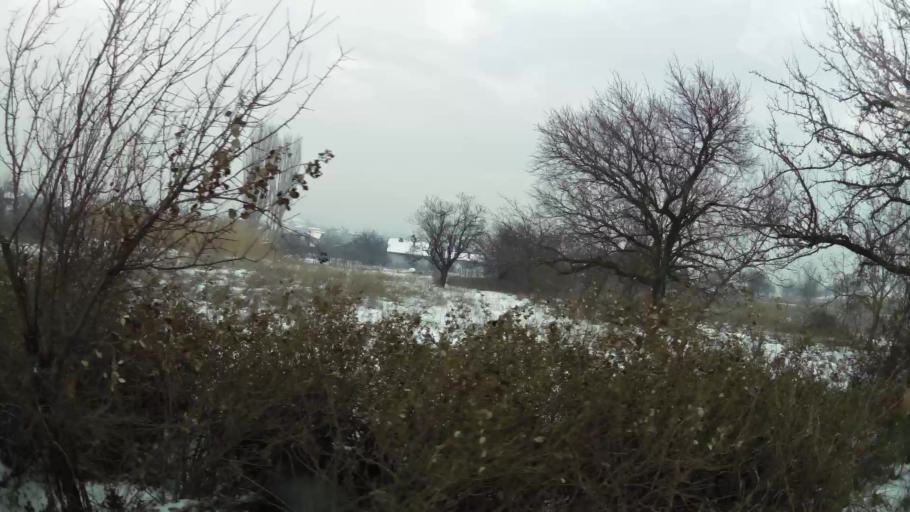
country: MK
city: Kondovo
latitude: 42.0354
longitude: 21.3383
